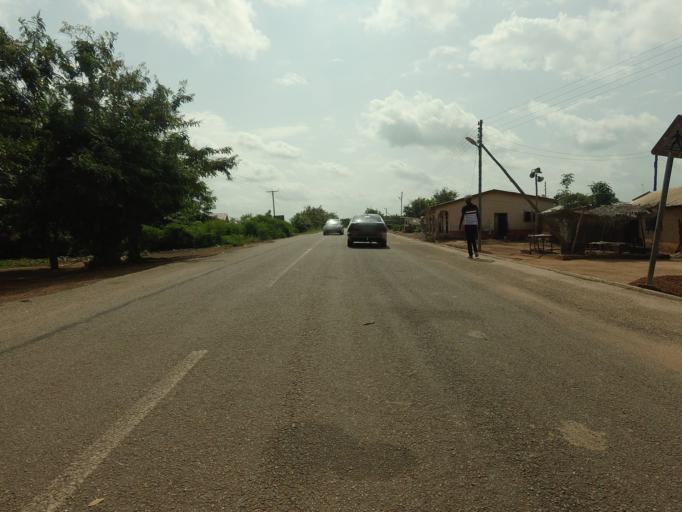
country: TG
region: Maritime
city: Lome
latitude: 6.2682
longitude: 0.9481
